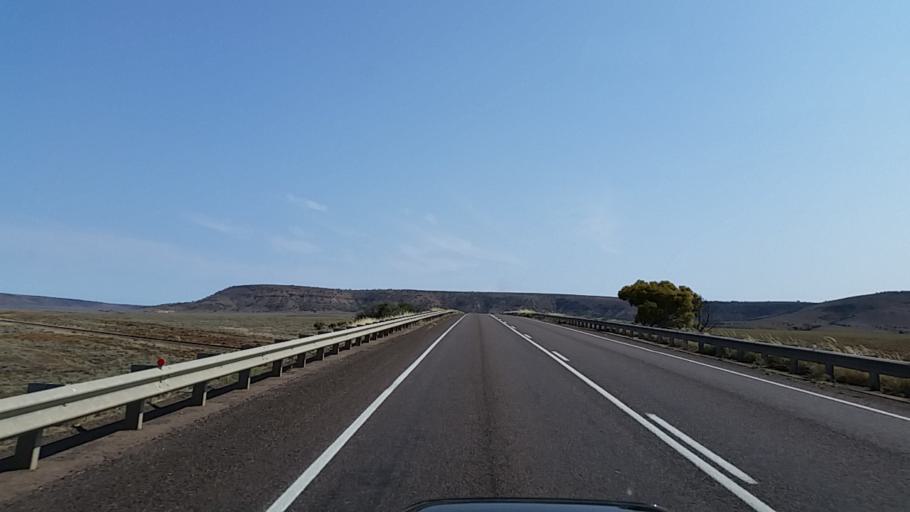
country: AU
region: South Australia
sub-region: Port Augusta
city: Port Augusta West
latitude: -32.5430
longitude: 137.6407
